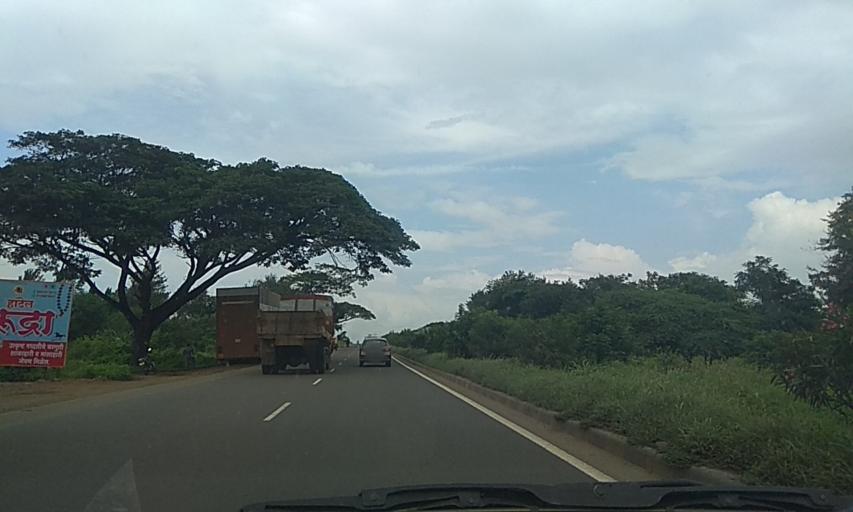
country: IN
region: Maharashtra
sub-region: Kolhapur
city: Kolhapur
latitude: 16.7834
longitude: 74.2781
